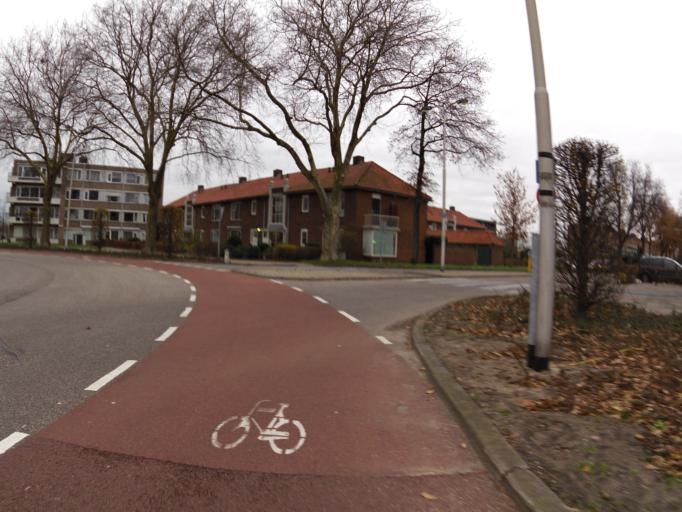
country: NL
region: North Brabant
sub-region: Gemeente Oss
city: Oss
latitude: 51.7576
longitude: 5.5373
